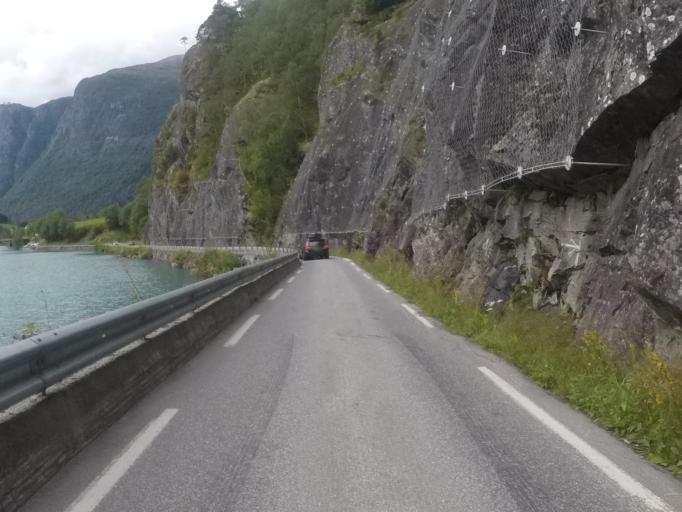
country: NO
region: Sogn og Fjordane
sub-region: Stryn
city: Stryn
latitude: 61.8575
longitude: 6.8950
